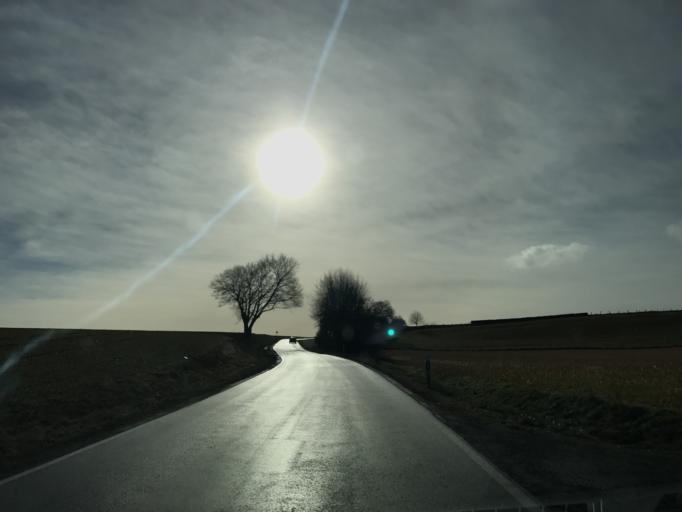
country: DE
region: Hesse
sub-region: Regierungsbezirk Kassel
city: Hofgeismar
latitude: 51.5139
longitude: 9.3876
